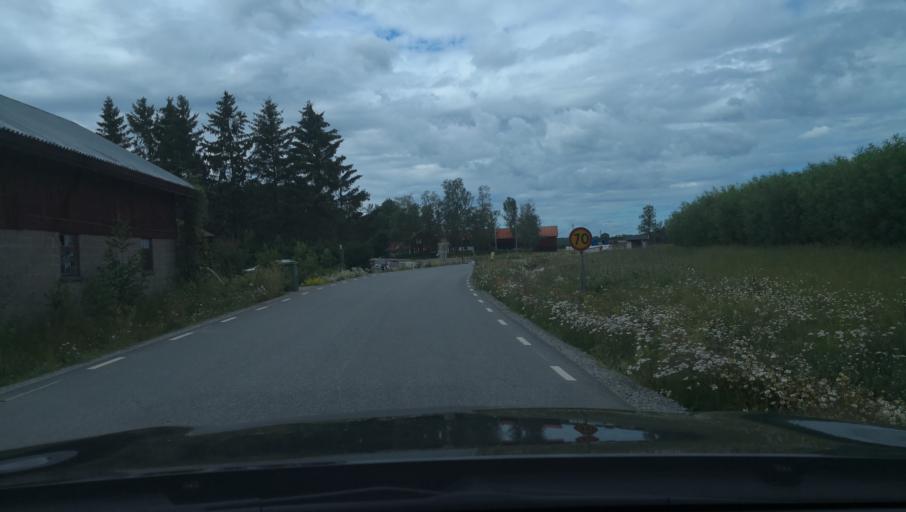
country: SE
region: Vaestmanland
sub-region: Hallstahammars Kommun
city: Hallstahammar
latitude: 59.5992
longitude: 16.1504
